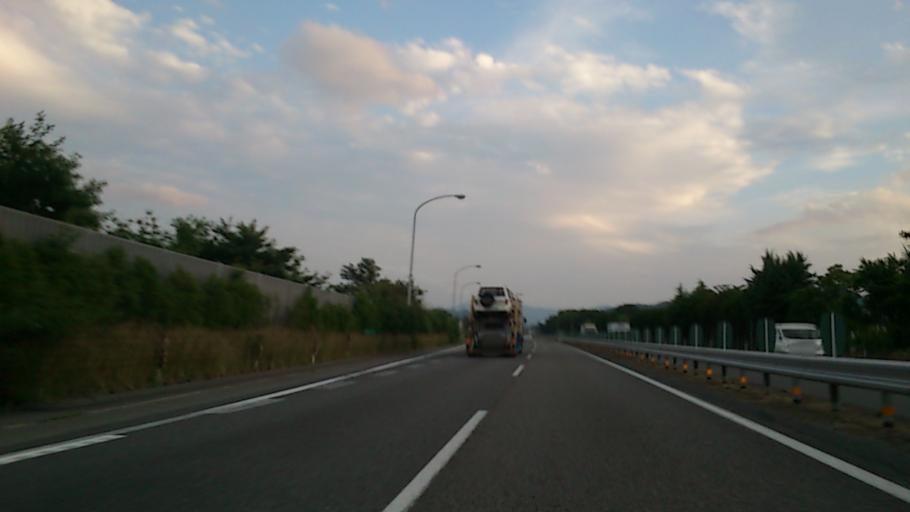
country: JP
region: Nagano
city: Iida
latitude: 35.5027
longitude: 137.7971
